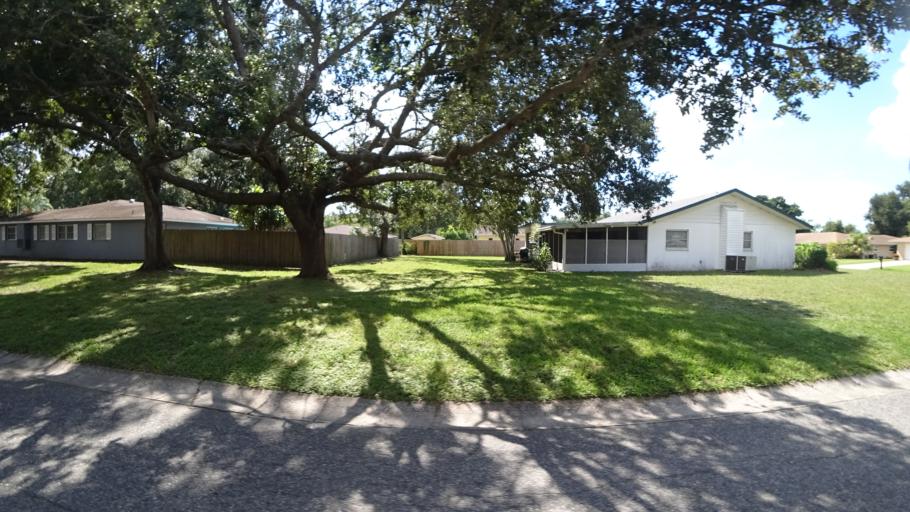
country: US
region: Florida
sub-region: Manatee County
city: Whitfield
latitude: 27.4147
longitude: -82.5603
